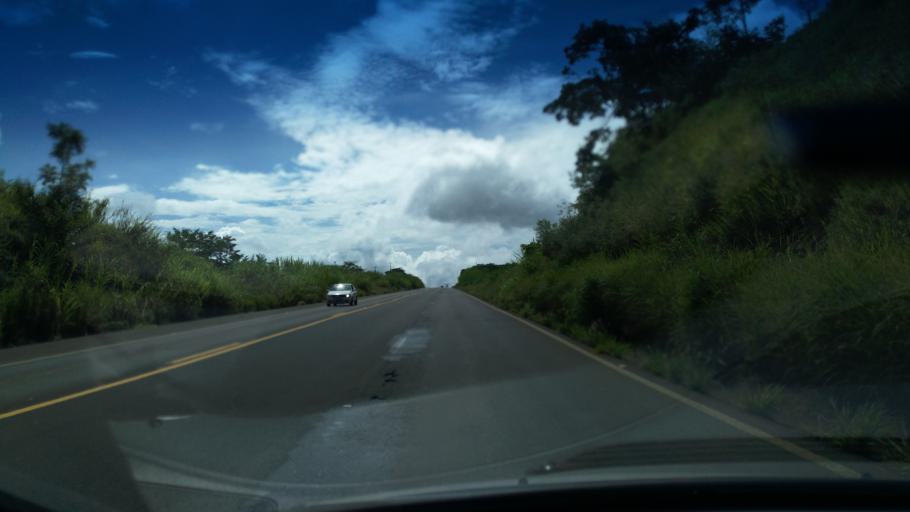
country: BR
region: Sao Paulo
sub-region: Santo Antonio Do Jardim
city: Espirito Santo do Pinhal
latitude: -22.1567
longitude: -46.7263
